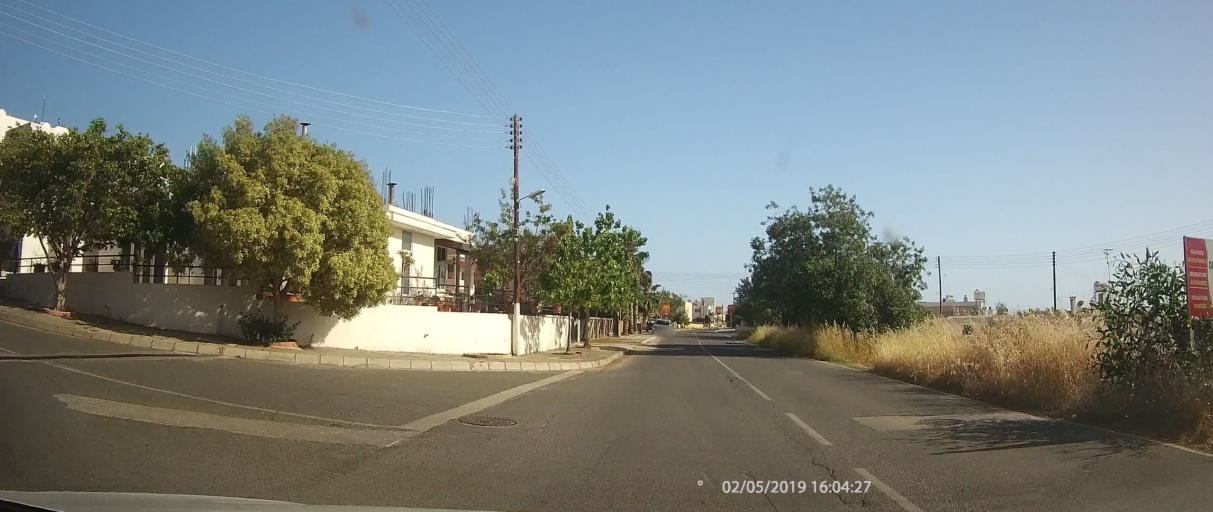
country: CY
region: Pafos
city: Empa
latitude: 34.8192
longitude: 32.4228
